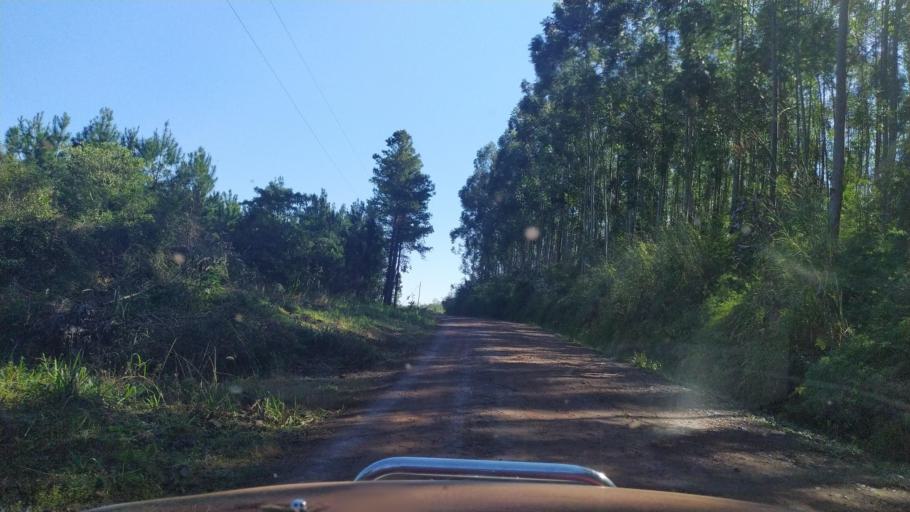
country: AR
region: Misiones
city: El Alcazar
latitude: -26.7191
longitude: -54.6903
